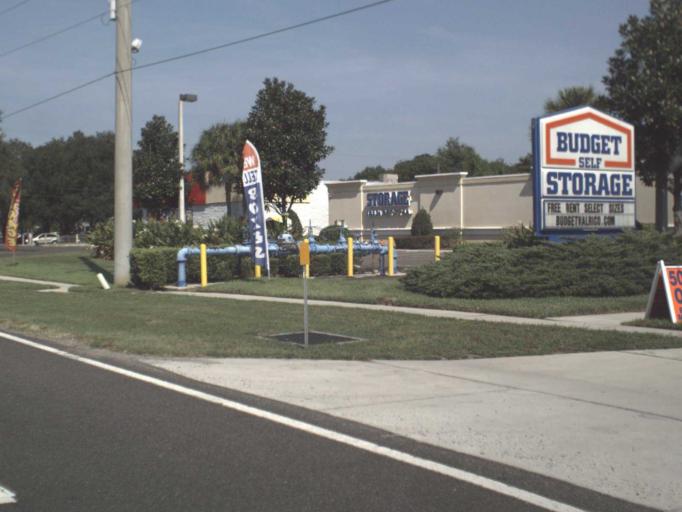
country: US
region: Florida
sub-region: Hillsborough County
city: Valrico
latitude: 27.9380
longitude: -82.2434
